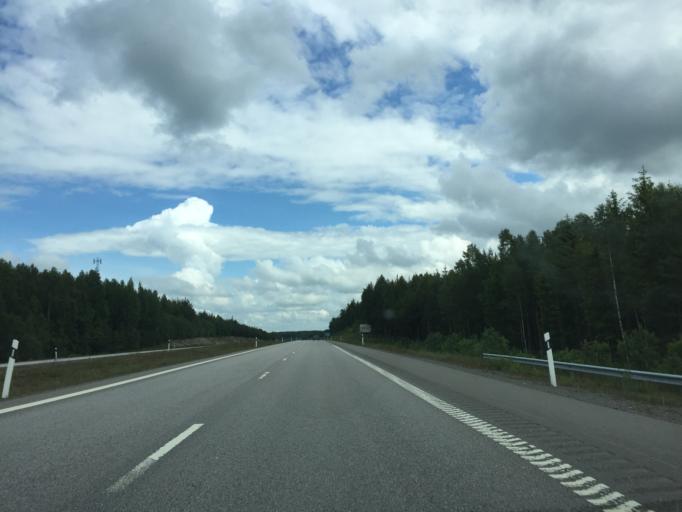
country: SE
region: OErebro
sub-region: Lindesbergs Kommun
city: Fellingsbro
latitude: 59.3891
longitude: 15.6842
